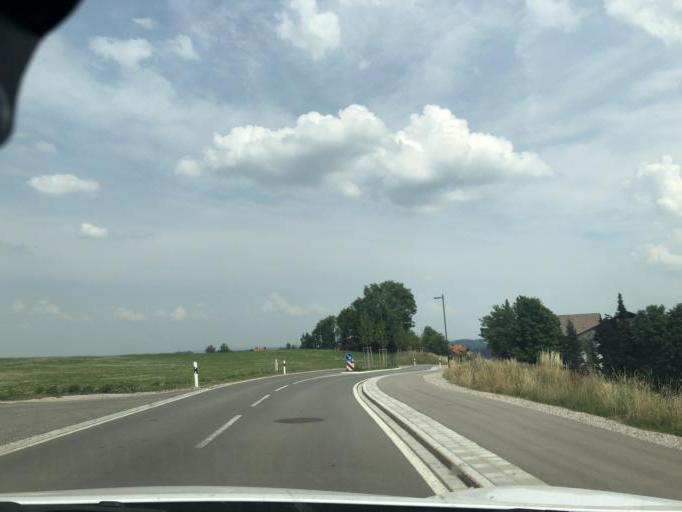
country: DE
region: Bavaria
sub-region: Swabia
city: Oy-Mittelberg
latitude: 47.6435
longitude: 10.4462
